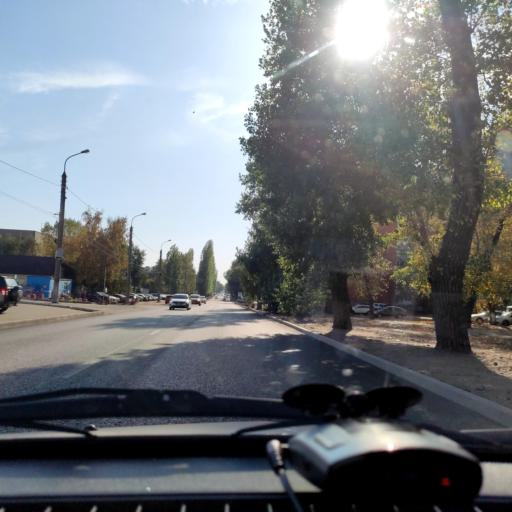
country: RU
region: Voronezj
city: Voronezh
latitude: 51.6492
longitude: 39.2446
